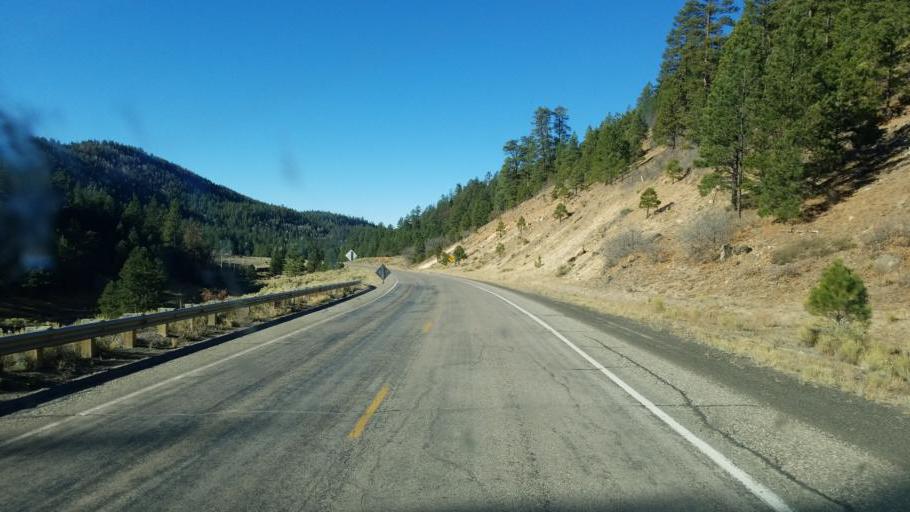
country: US
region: New Mexico
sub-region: McKinley County
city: Navajo
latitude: 36.0864
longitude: -108.8784
